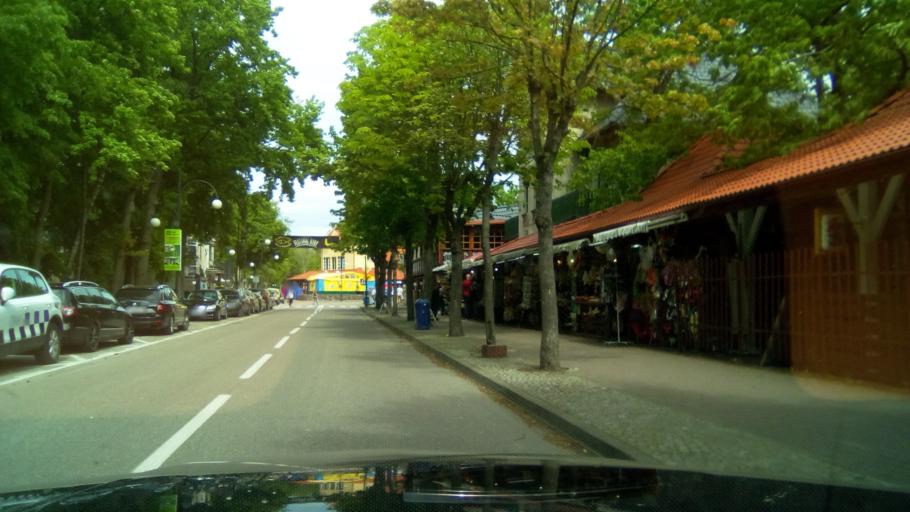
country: PL
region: Pomeranian Voivodeship
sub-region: Powiat leborski
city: Leba
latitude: 54.7642
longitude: 17.5572
